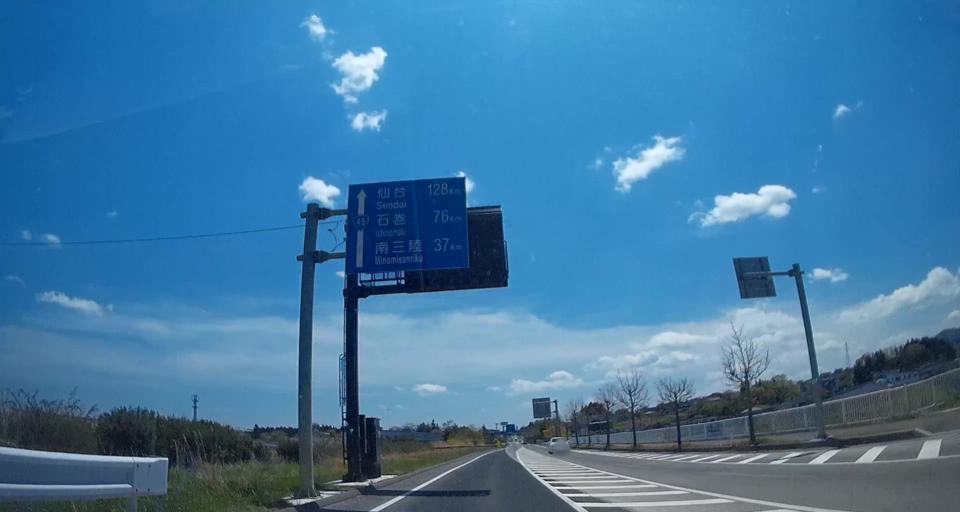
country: JP
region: Iwate
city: Ofunato
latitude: 38.8702
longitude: 141.5784
